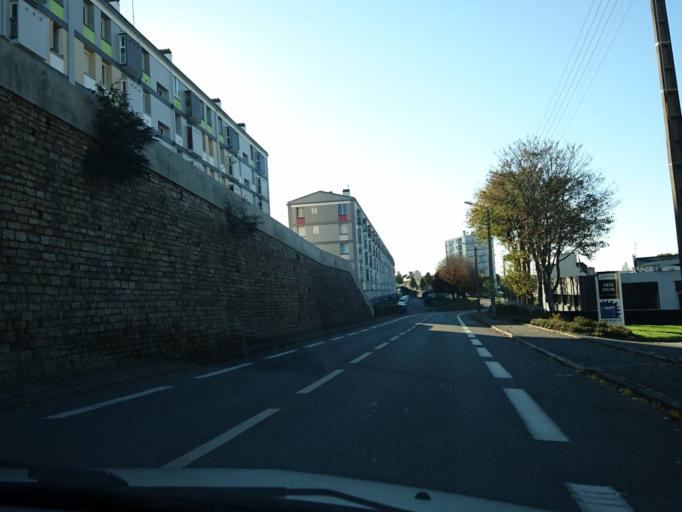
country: FR
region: Brittany
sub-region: Departement du Finistere
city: Brest
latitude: 48.4073
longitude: -4.4734
